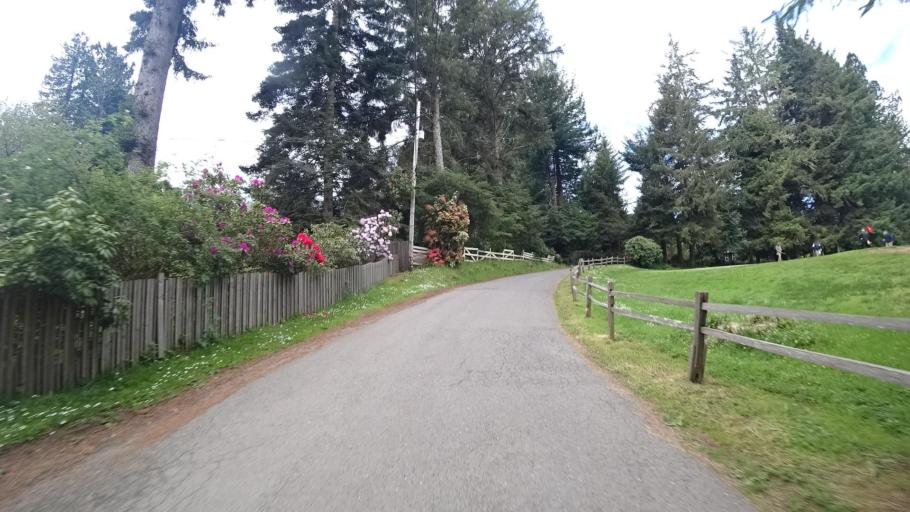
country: US
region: California
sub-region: Humboldt County
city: Bayside
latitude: 40.8460
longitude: -124.0530
